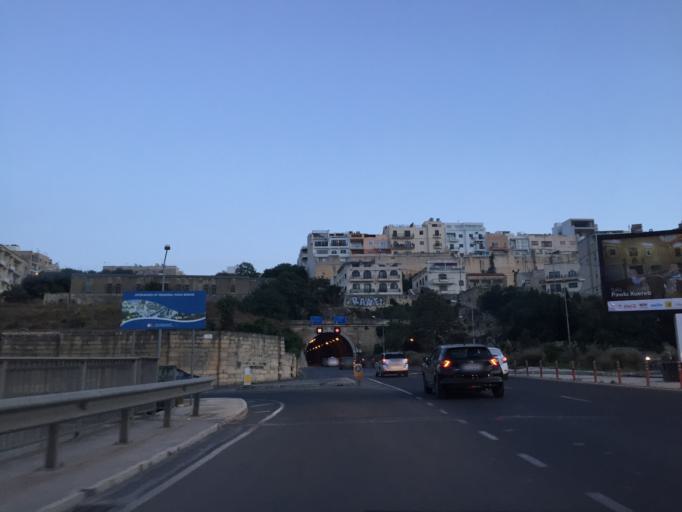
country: MT
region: Saint Julian
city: San Giljan
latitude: 35.9160
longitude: 14.4863
